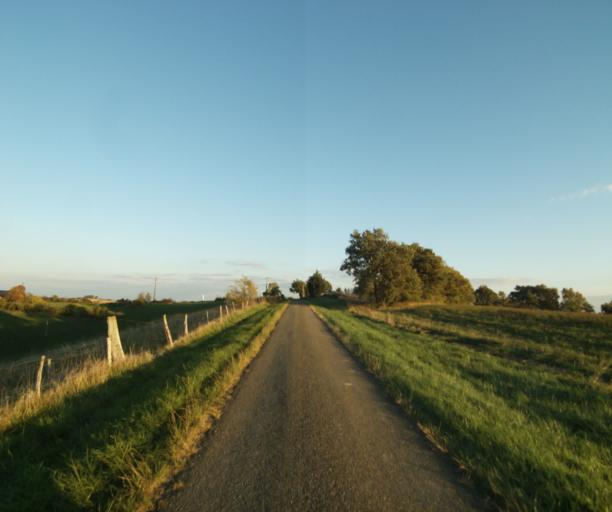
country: FR
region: Midi-Pyrenees
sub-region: Departement du Gers
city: Vic-Fezensac
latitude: 43.7412
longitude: 0.1939
